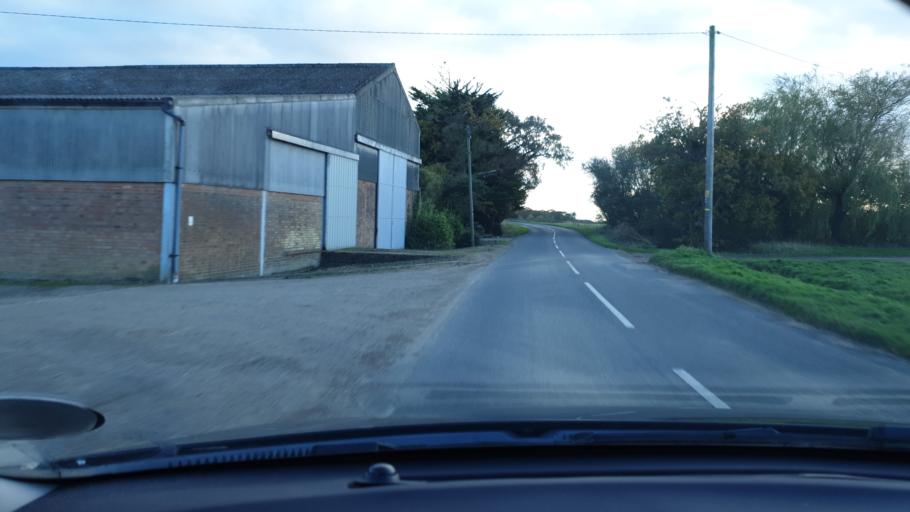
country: GB
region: England
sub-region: Essex
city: Mistley
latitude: 51.9040
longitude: 1.1433
